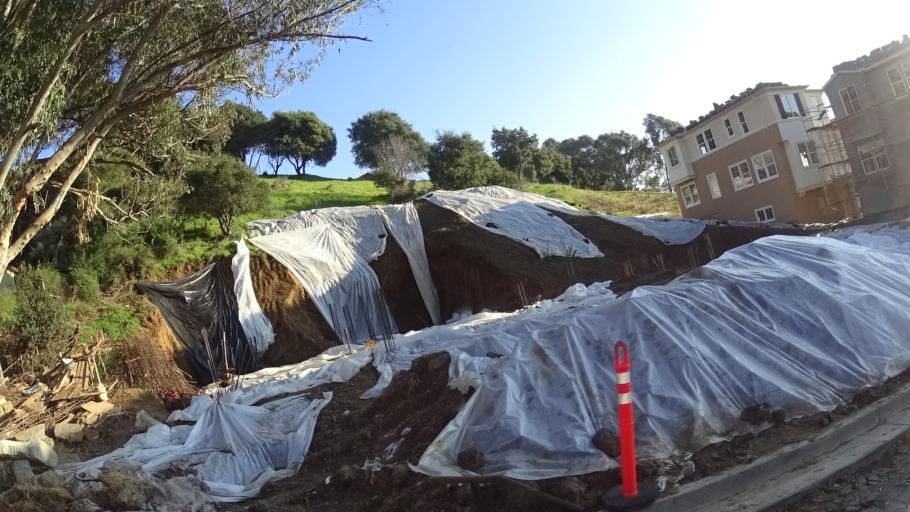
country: US
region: California
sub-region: Alameda County
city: Fairview
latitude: 37.6578
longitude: -122.0482
